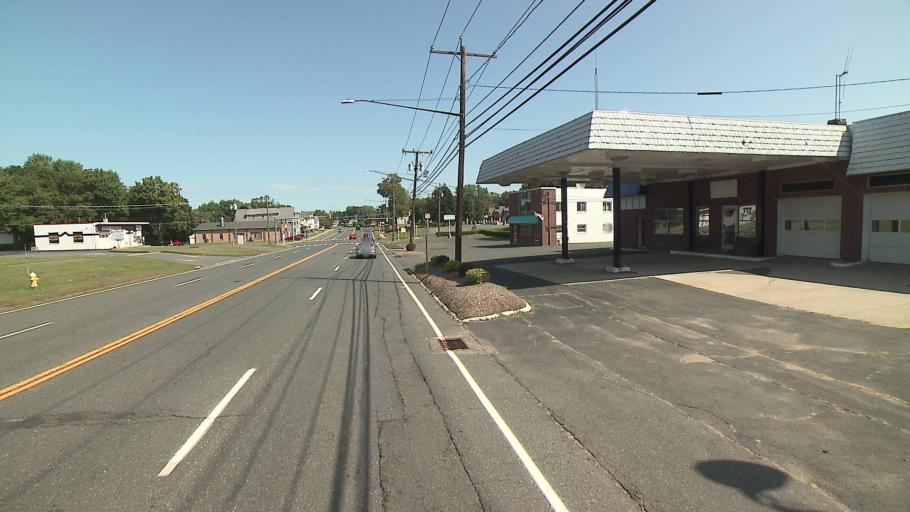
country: US
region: Connecticut
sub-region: Hartford County
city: Thompsonville
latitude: 42.0016
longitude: -72.5935
